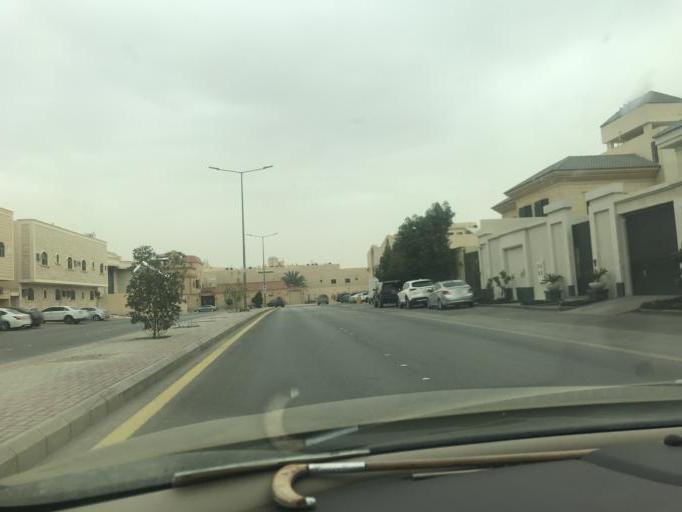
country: SA
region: Ar Riyad
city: Riyadh
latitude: 24.7364
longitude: 46.7571
